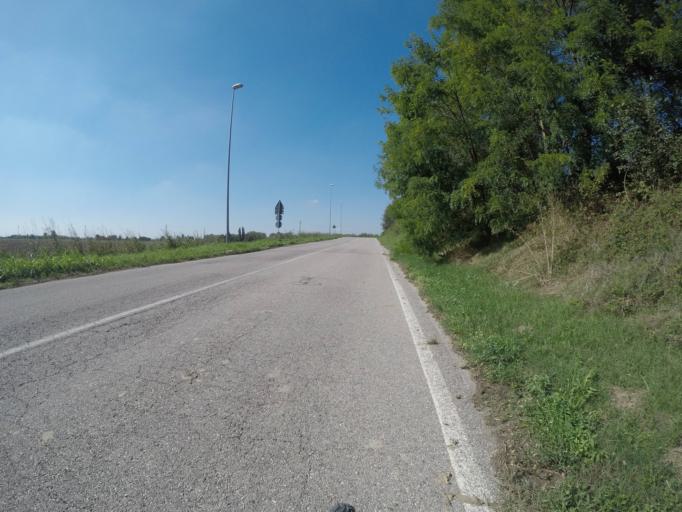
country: IT
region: Veneto
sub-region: Provincia di Rovigo
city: Arqua Polesine
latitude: 44.9973
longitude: 11.7424
